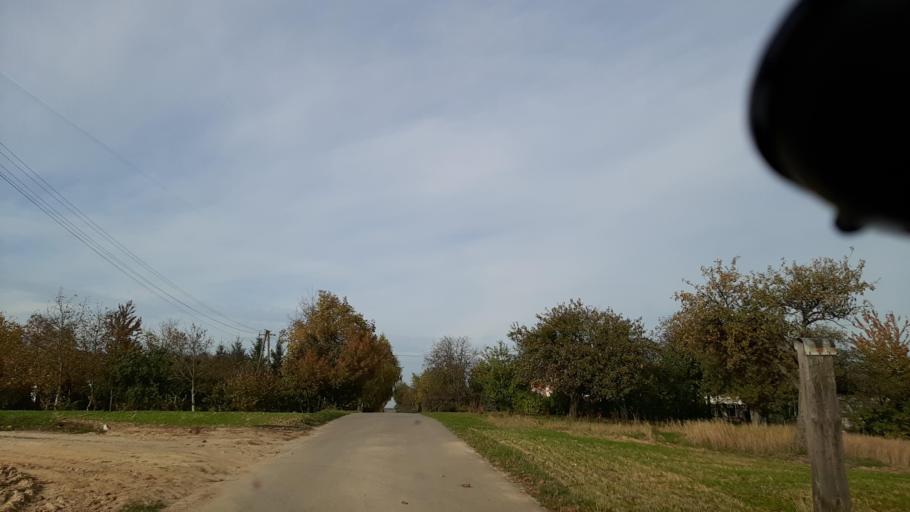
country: PL
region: Lublin Voivodeship
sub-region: Powiat lubelski
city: Jastkow
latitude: 51.3328
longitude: 22.4112
